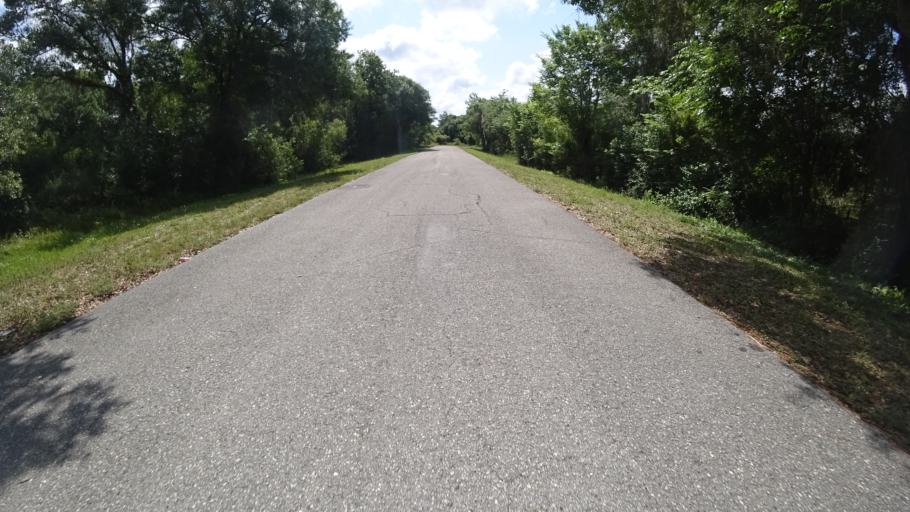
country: US
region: Florida
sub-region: Sarasota County
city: Lake Sarasota
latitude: 27.3481
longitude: -82.1559
